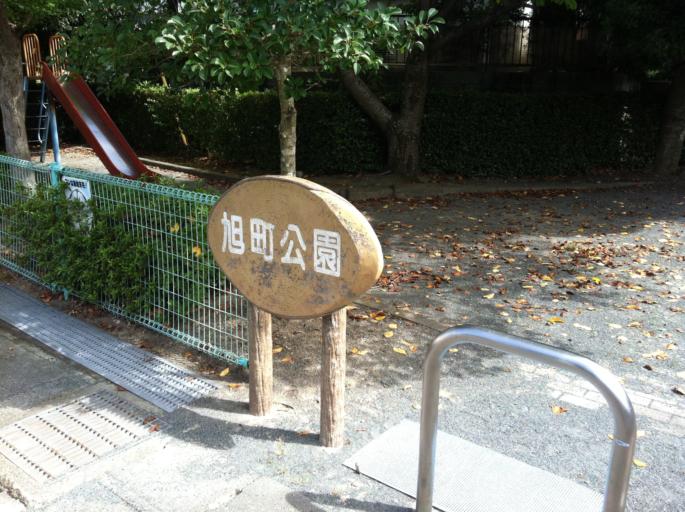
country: JP
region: Shizuoka
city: Kakegawa
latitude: 34.7791
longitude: 138.0230
